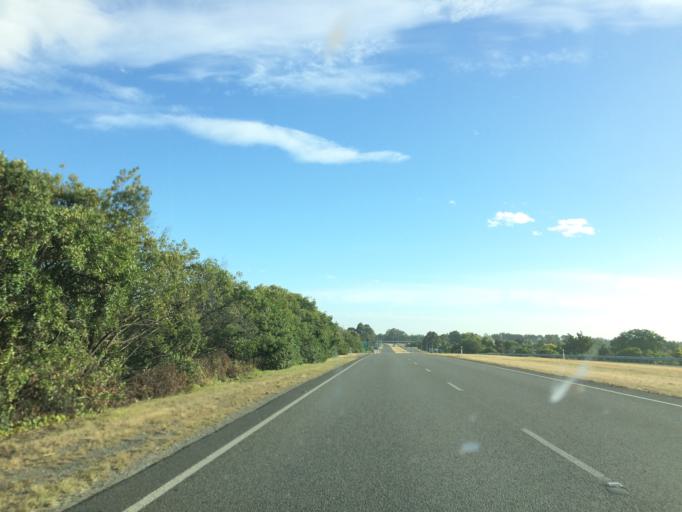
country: NZ
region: Canterbury
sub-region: Waimakariri District
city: Kaiapoi
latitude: -43.3789
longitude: 172.6448
